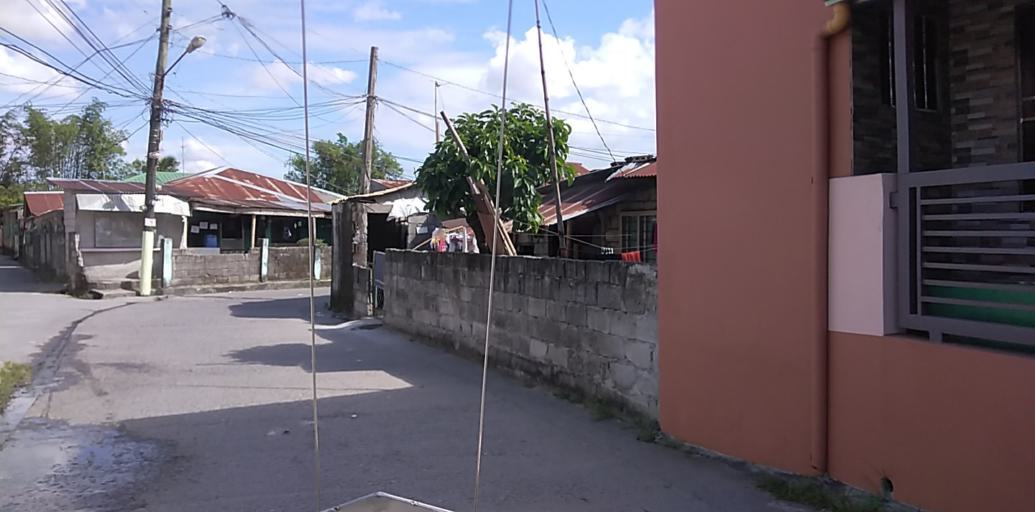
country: PH
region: Central Luzon
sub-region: Province of Pampanga
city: Porac
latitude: 15.0765
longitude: 120.5326
